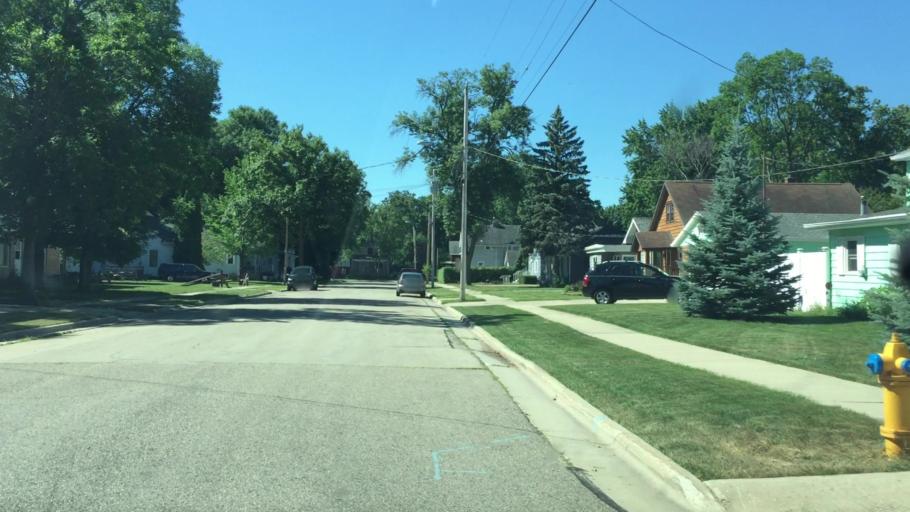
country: US
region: Wisconsin
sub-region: Winnebago County
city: Menasha
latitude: 44.1935
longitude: -88.4459
